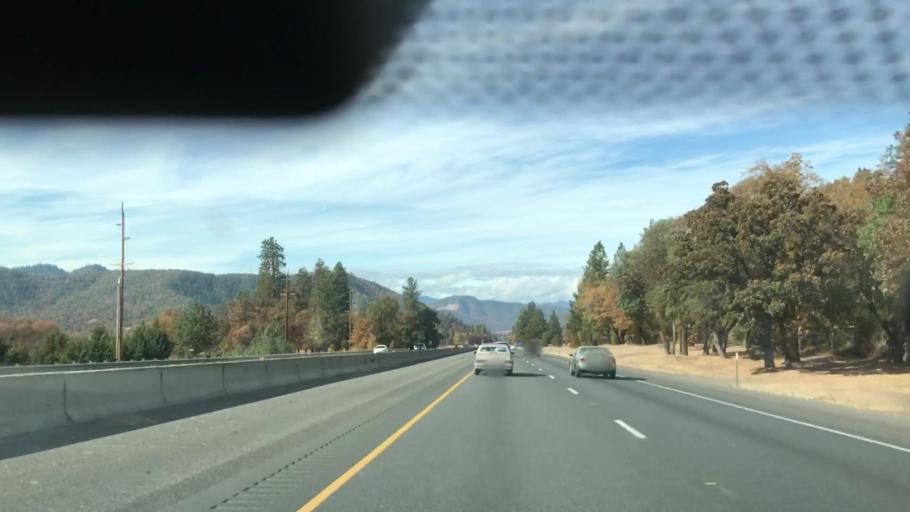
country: US
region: Oregon
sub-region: Jackson County
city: Gold Hill
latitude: 42.4178
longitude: -123.0105
